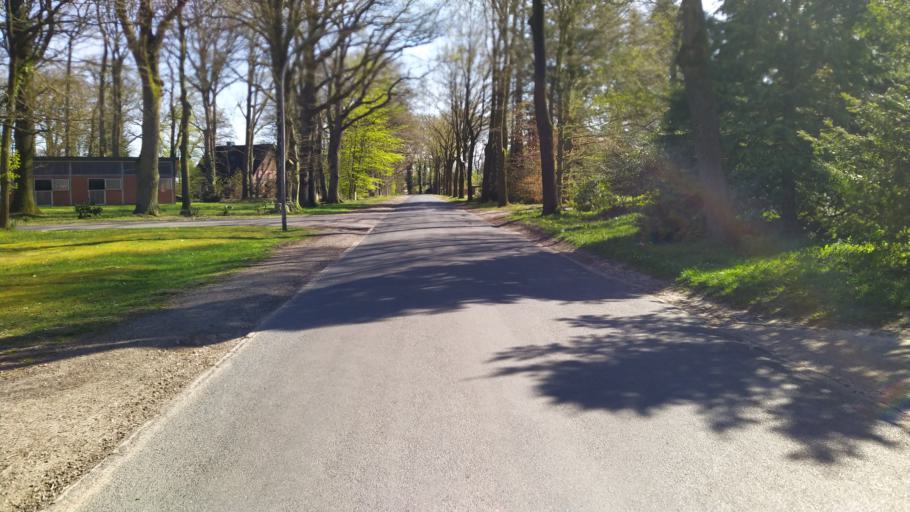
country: DE
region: Lower Saxony
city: Heeslingen
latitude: 53.3027
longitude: 9.3837
